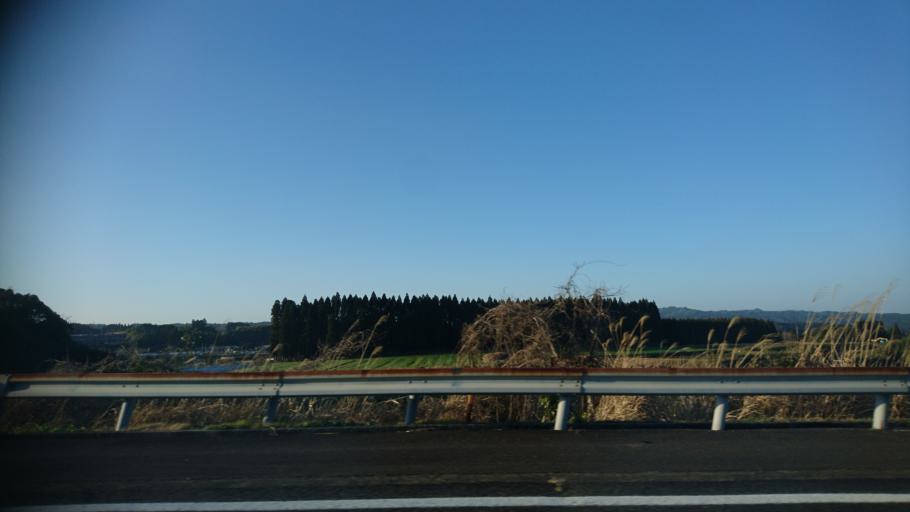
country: JP
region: Miyazaki
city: Miyazaki-shi
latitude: 31.8187
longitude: 131.2742
